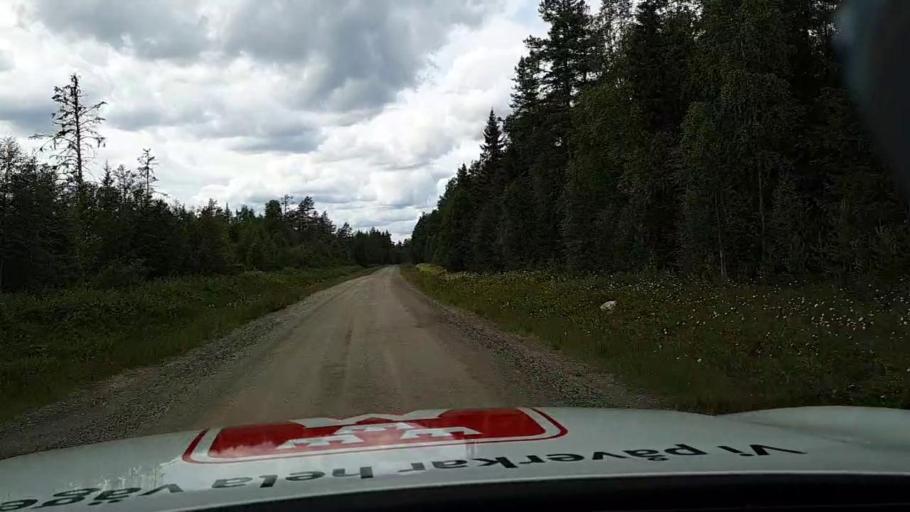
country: SE
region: Jaemtland
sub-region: Stroemsunds Kommun
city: Stroemsund
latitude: 63.3158
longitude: 15.4894
